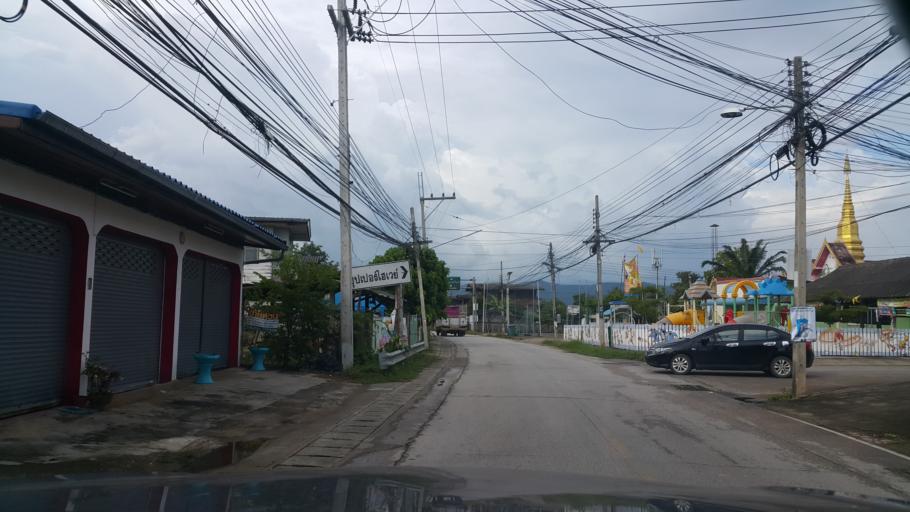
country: TH
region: Lampang
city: Thoen
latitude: 17.6216
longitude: 99.2253
